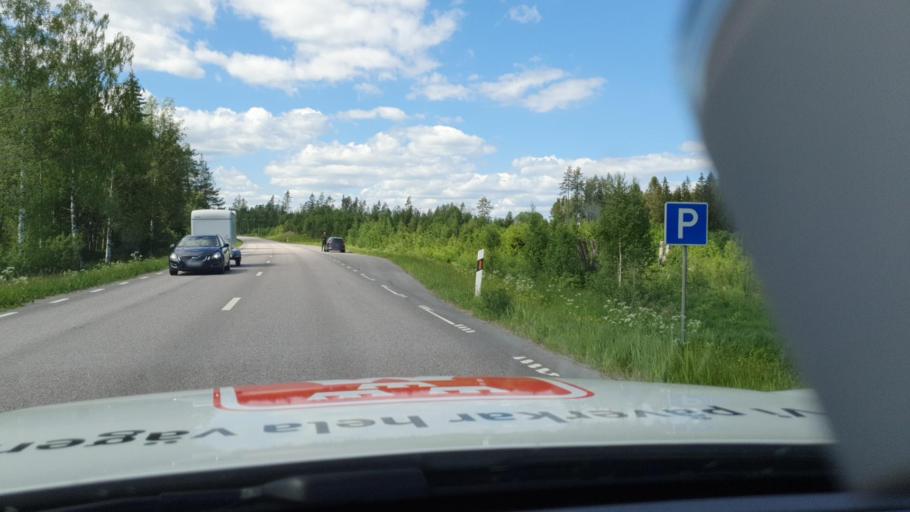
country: SE
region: Uppsala
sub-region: Tierps Kommun
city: Karlholmsbruk
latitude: 60.5315
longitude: 17.5868
